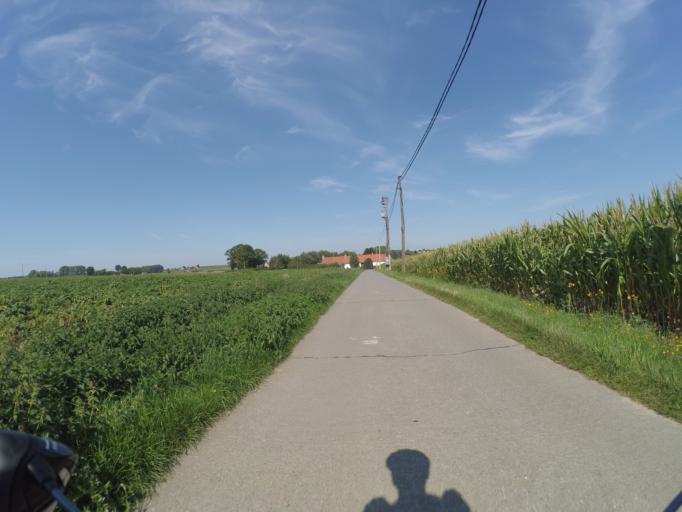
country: BE
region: Flanders
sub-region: Provincie Oost-Vlaanderen
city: Kruishoutem
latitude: 50.8464
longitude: 3.5485
